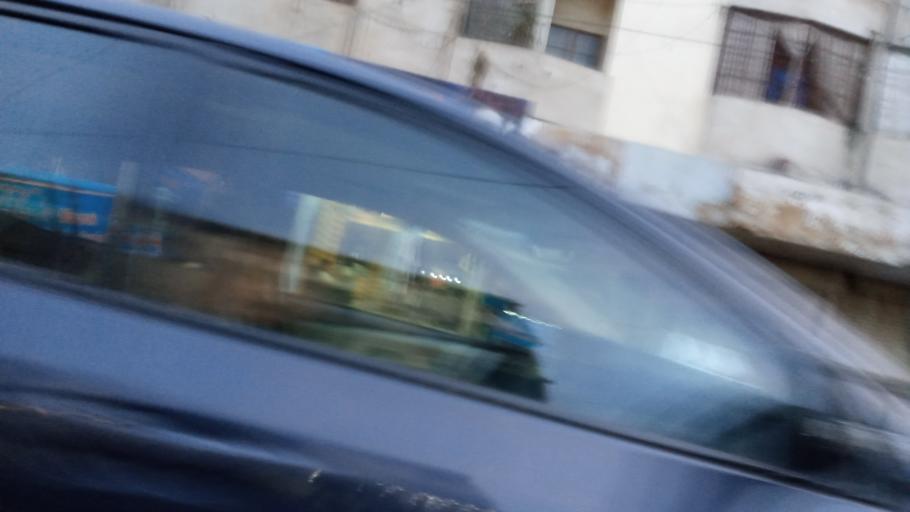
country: PK
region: Sindh
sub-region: Karachi District
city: Karachi
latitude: 24.9397
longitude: 67.0813
